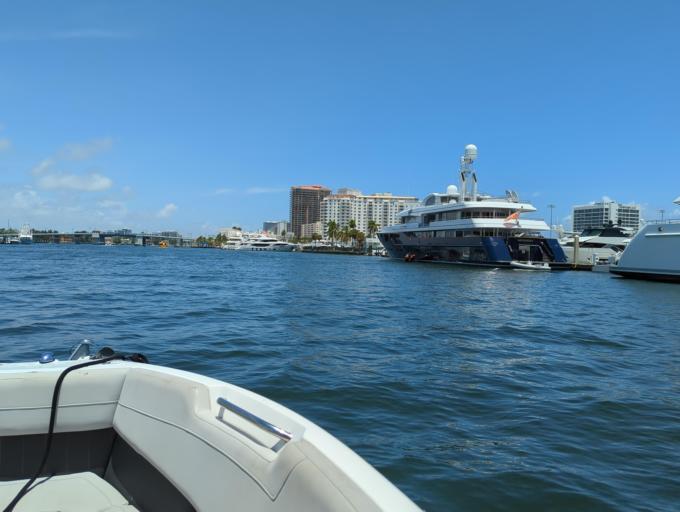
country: US
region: Florida
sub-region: Broward County
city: Sunrise
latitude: 26.1141
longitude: -80.1089
